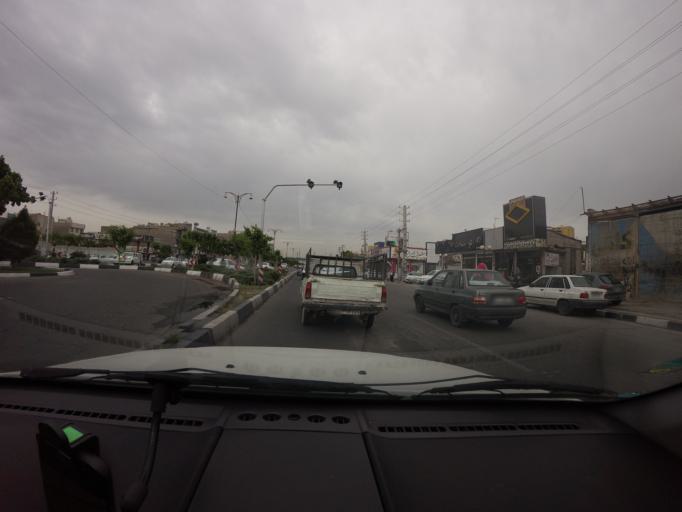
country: IR
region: Tehran
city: Eslamshahr
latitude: 35.5502
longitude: 51.2280
